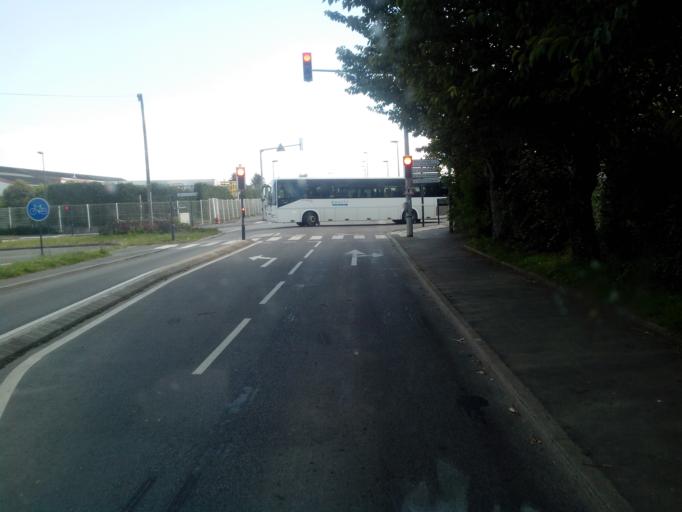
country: FR
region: Brittany
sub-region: Departement d'Ille-et-Vilaine
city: Noyal-sur-Vilaine
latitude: 48.1129
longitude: -1.5326
